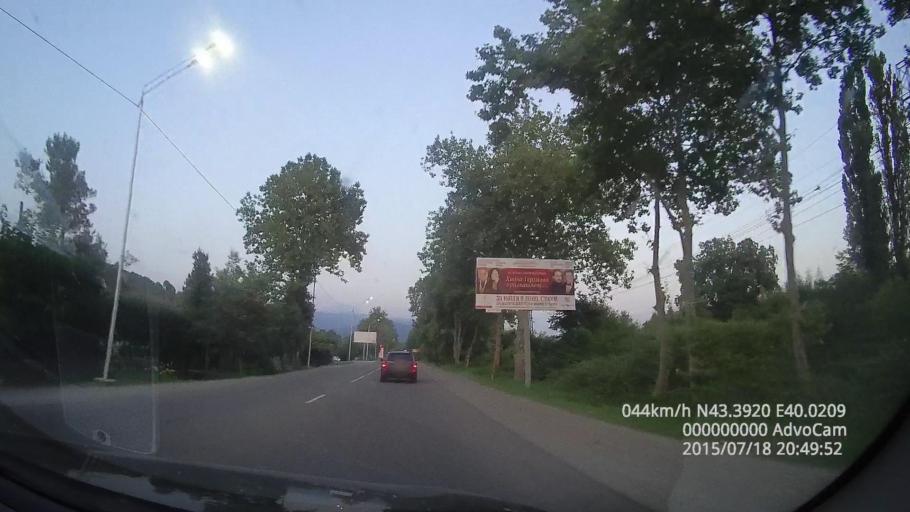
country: GE
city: Gantiadi
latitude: 43.3918
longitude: 40.0222
